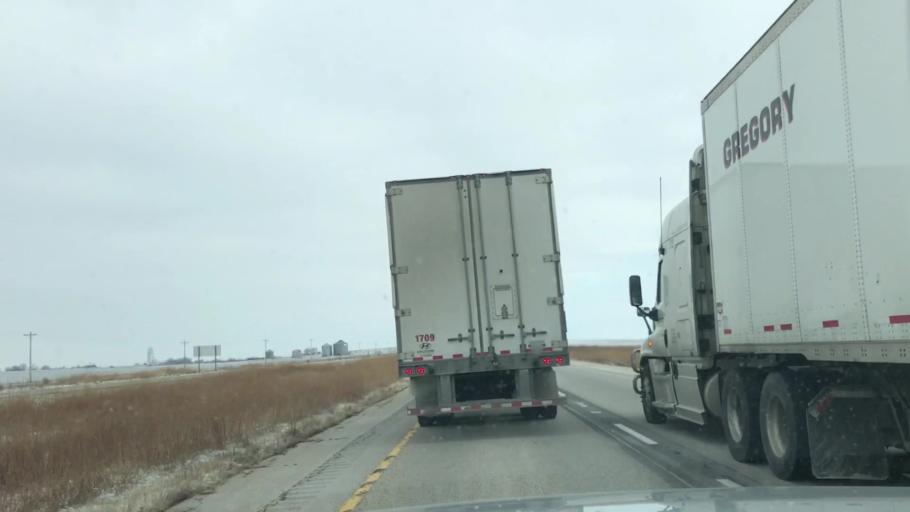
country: US
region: Illinois
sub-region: Sangamon County
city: Divernon
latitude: 39.4706
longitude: -89.6444
